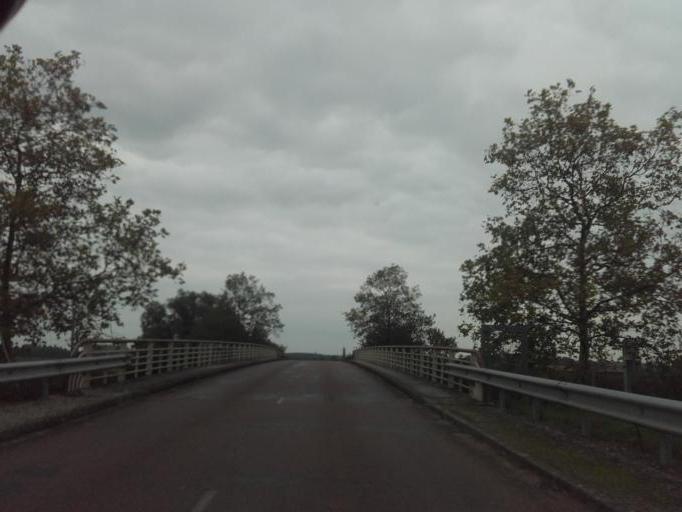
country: FR
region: Bourgogne
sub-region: Departement de la Cote-d'Or
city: Bligny-les-Beaune
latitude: 46.9892
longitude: 4.8522
